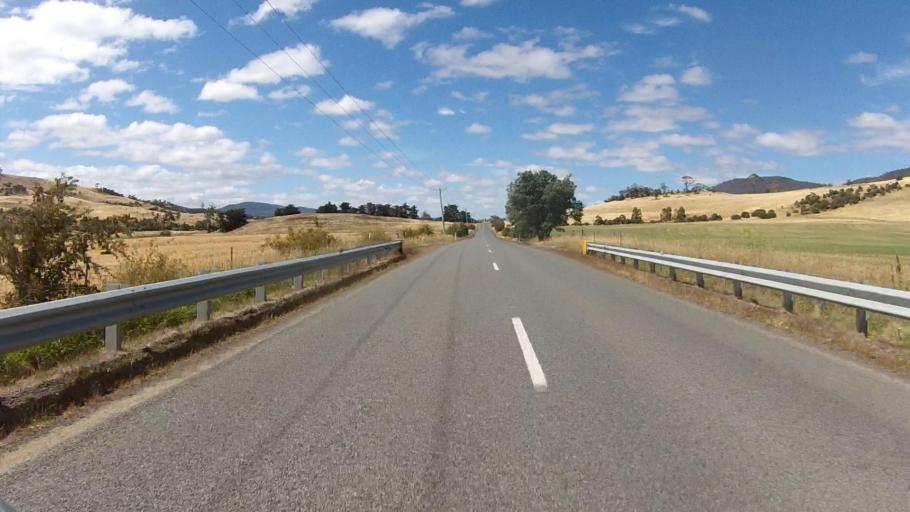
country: AU
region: Tasmania
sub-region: Brighton
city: Bridgewater
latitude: -42.5936
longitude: 147.4122
